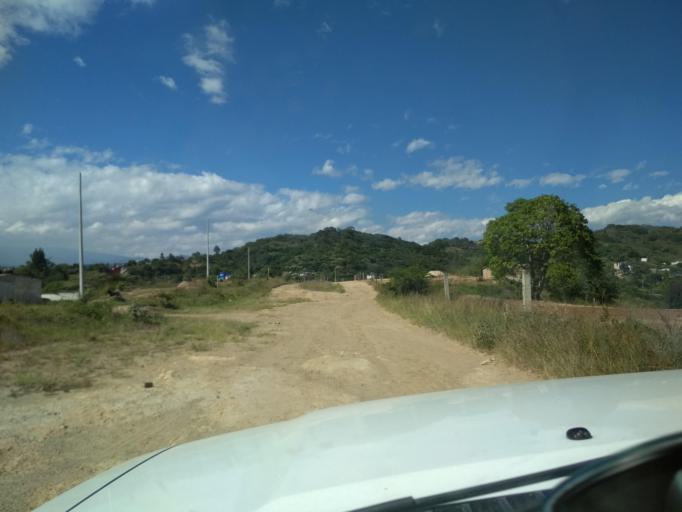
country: MX
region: Veracruz
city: El Castillo
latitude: 19.5482
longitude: -96.8555
